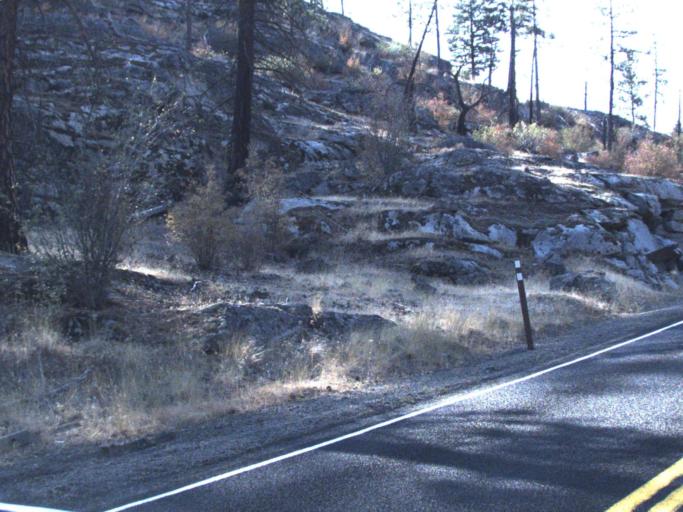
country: US
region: Washington
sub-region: Spokane County
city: Airway Heights
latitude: 47.8628
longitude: -117.7121
